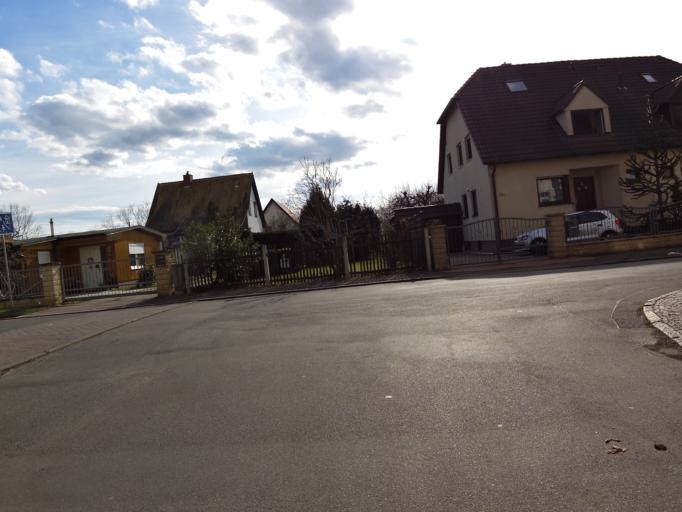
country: DE
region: Saxony
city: Taucha
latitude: 51.3345
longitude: 12.4754
